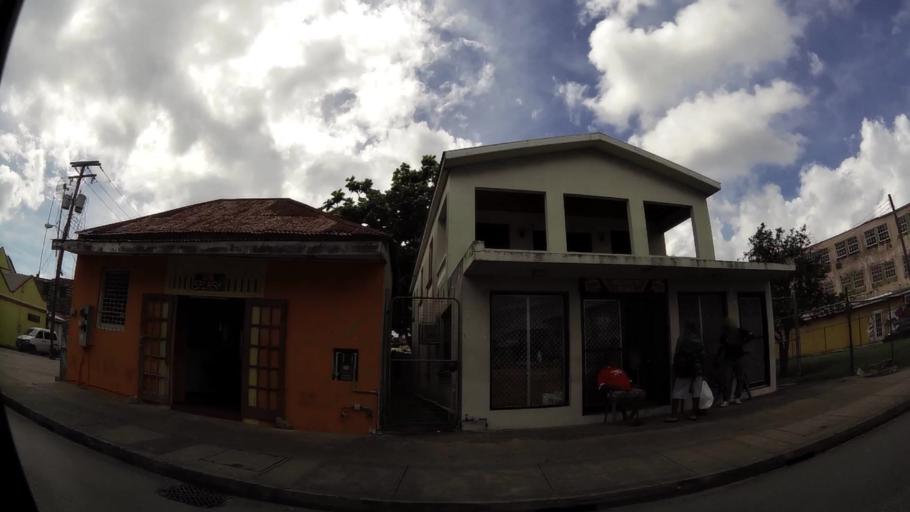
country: BB
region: Saint Michael
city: Bridgetown
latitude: 13.1019
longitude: -59.6176
